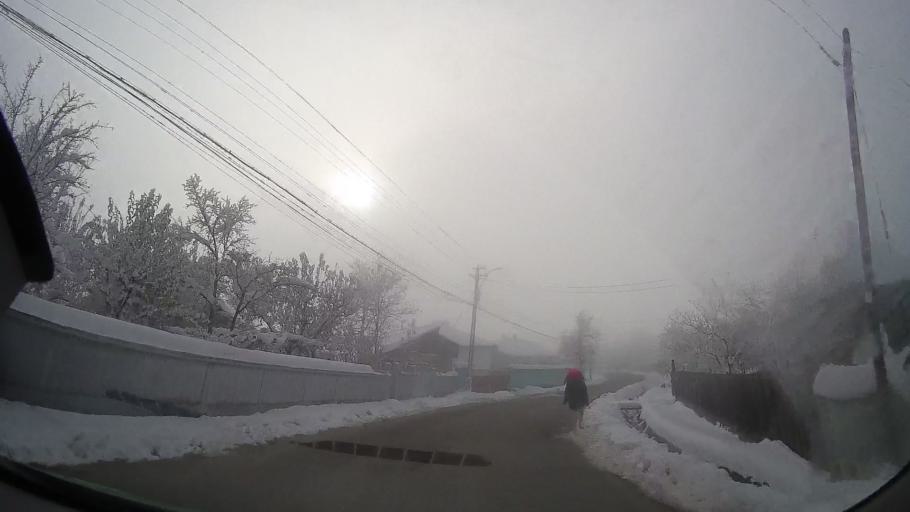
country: RO
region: Iasi
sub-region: Comuna Valea Seaca
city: Topile
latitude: 47.2591
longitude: 26.6669
